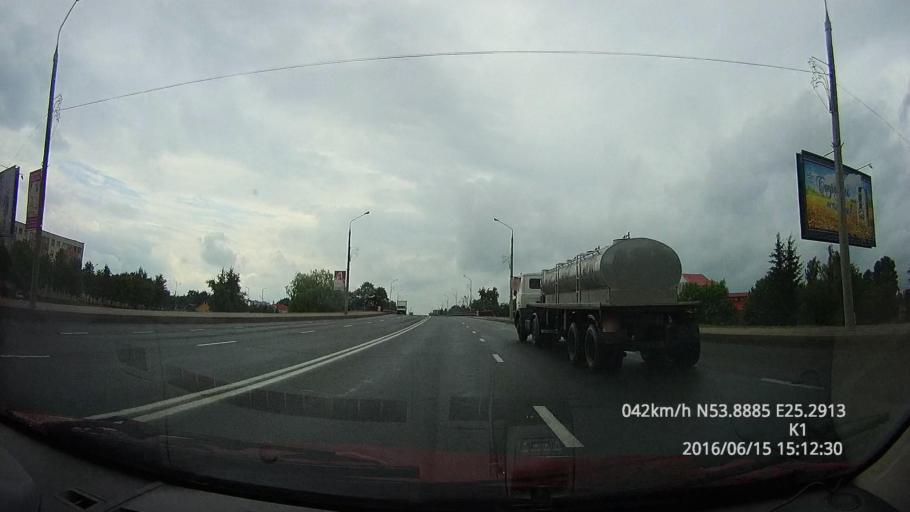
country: BY
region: Grodnenskaya
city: Lida
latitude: 53.8884
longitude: 25.2909
